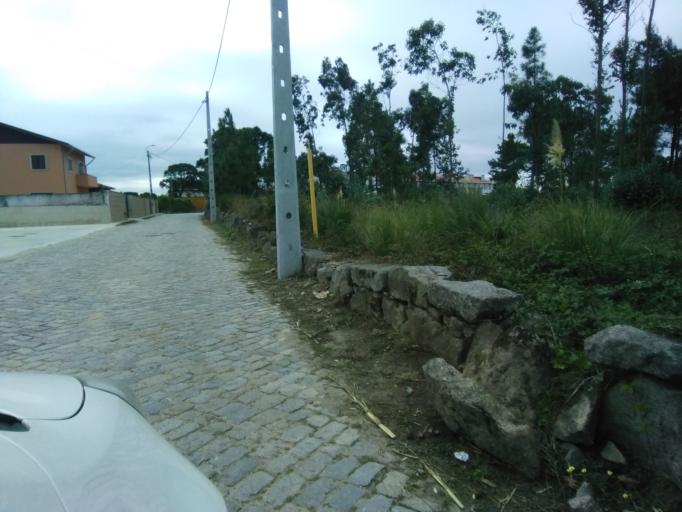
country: PT
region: Porto
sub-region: Matosinhos
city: Santa Cruz do Bispo
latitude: 41.2317
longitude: -8.7102
